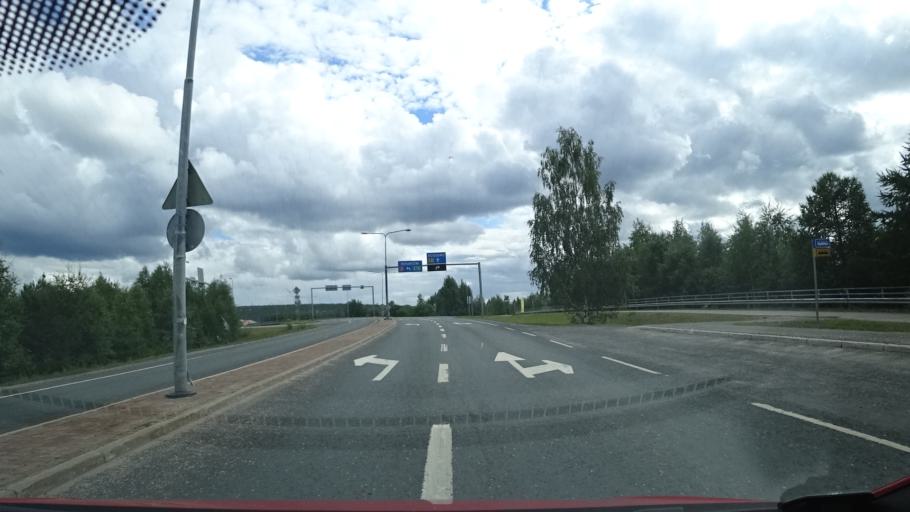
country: FI
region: Lapland
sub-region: Rovaniemi
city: Rovaniemi
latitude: 66.5204
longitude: 25.7472
